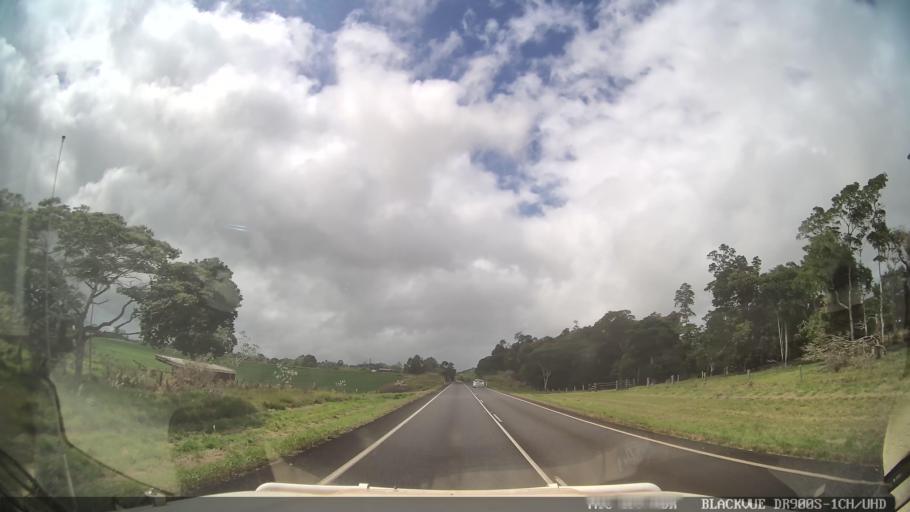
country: AU
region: Queensland
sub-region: Tablelands
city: Atherton
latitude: -17.3038
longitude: 145.6233
